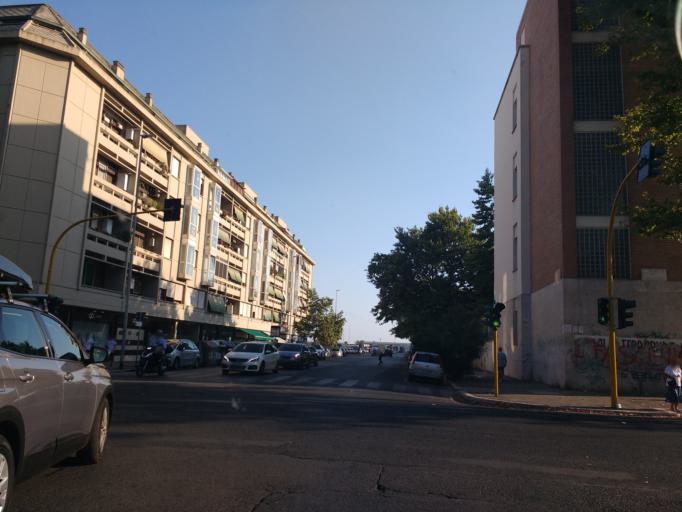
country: IT
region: Latium
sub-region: Citta metropolitana di Roma Capitale
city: Lido di Ostia
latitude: 41.7333
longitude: 12.2738
